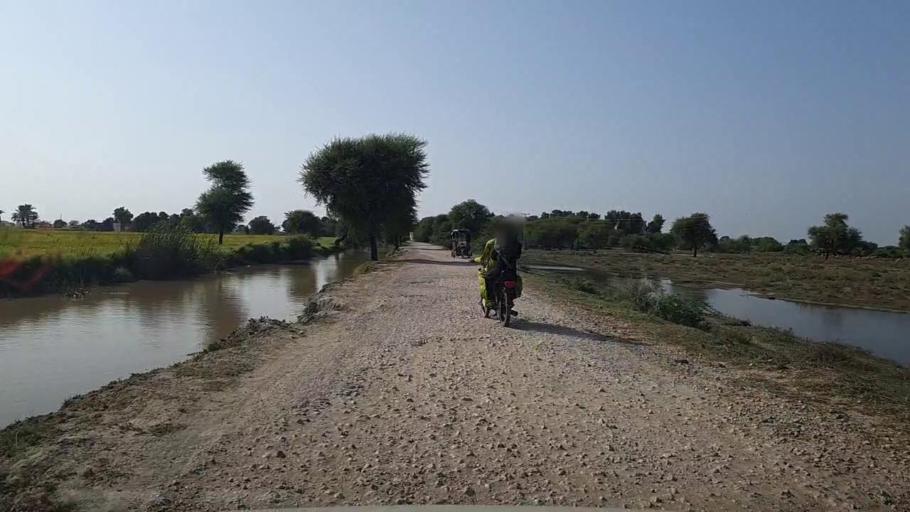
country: PK
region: Sindh
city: Kario
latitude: 24.8042
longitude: 68.5494
